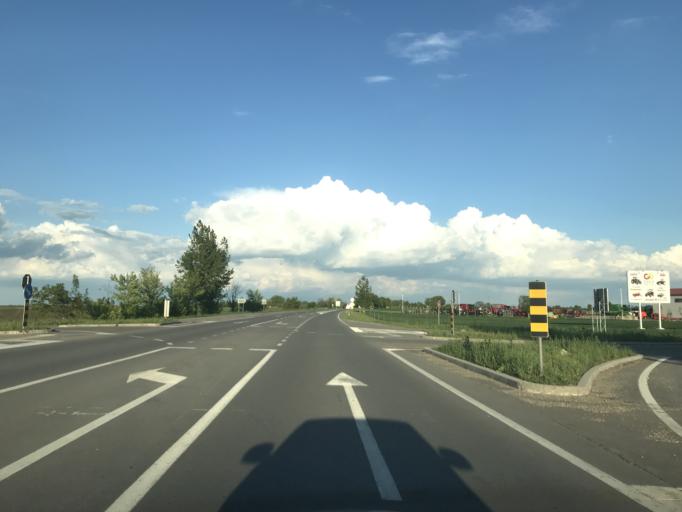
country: RS
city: Aradac
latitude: 45.3920
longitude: 20.2969
